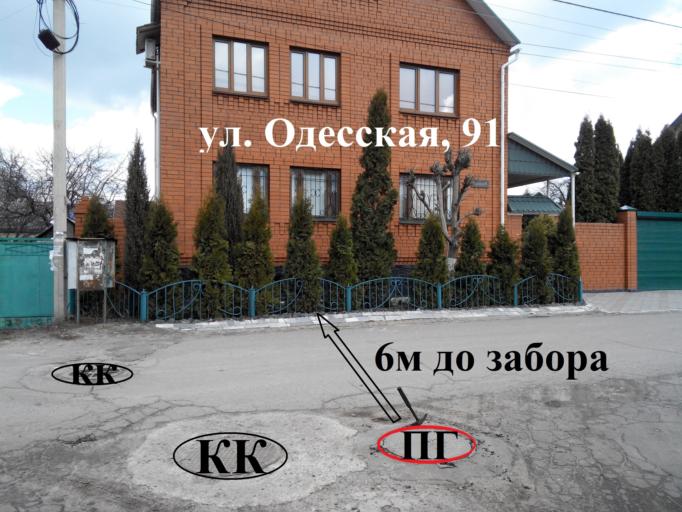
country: RU
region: Voronezj
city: Voronezh
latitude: 51.6346
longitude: 39.1652
